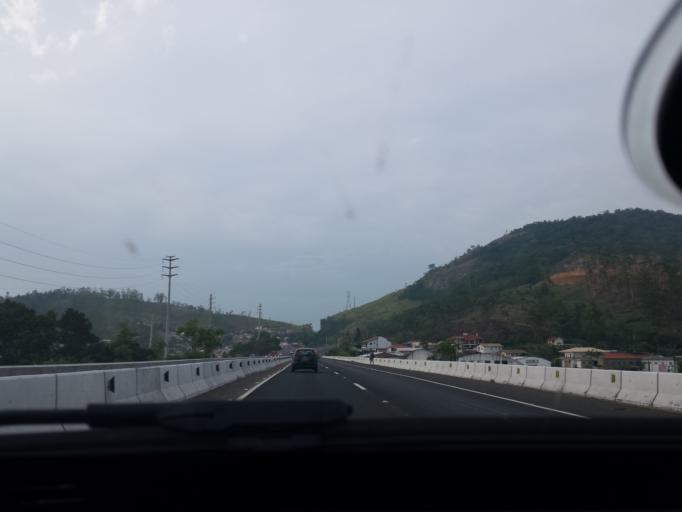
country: BR
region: Santa Catarina
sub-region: Tubarao
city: Tubarao
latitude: -28.4809
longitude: -49.0345
